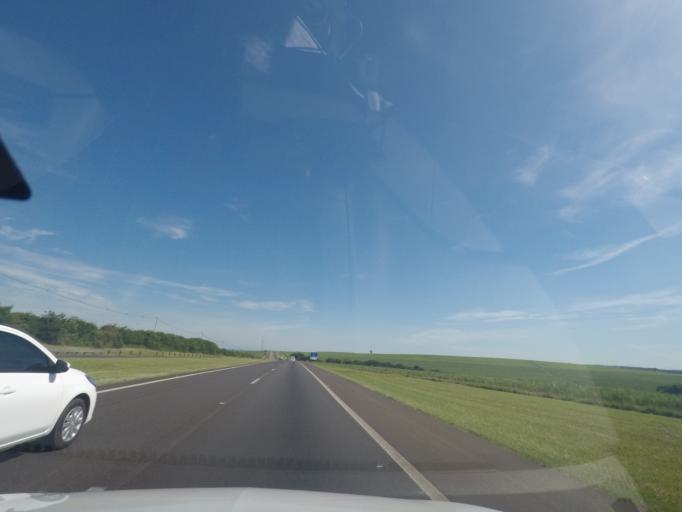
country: BR
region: Sao Paulo
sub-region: Itirapina
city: Itirapina
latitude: -22.2077
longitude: -47.7700
